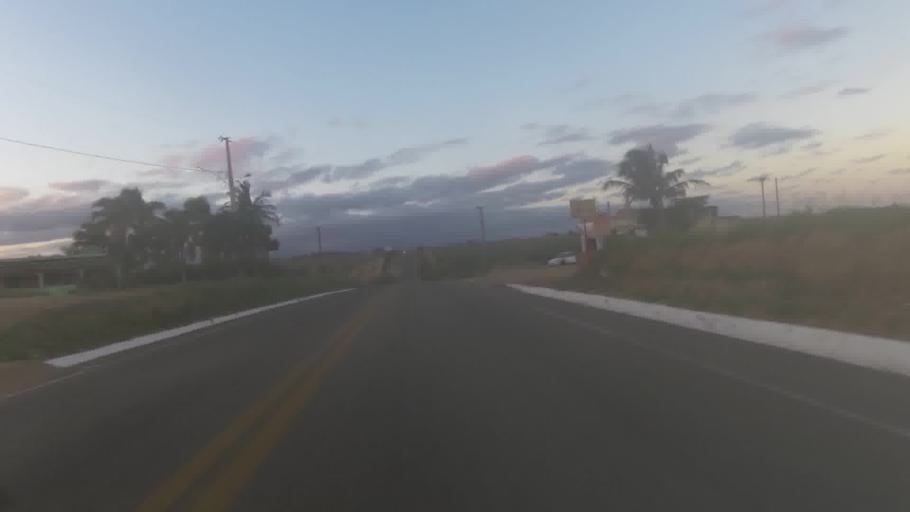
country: BR
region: Espirito Santo
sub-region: Marataizes
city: Marataizes
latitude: -21.0616
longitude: -40.8498
